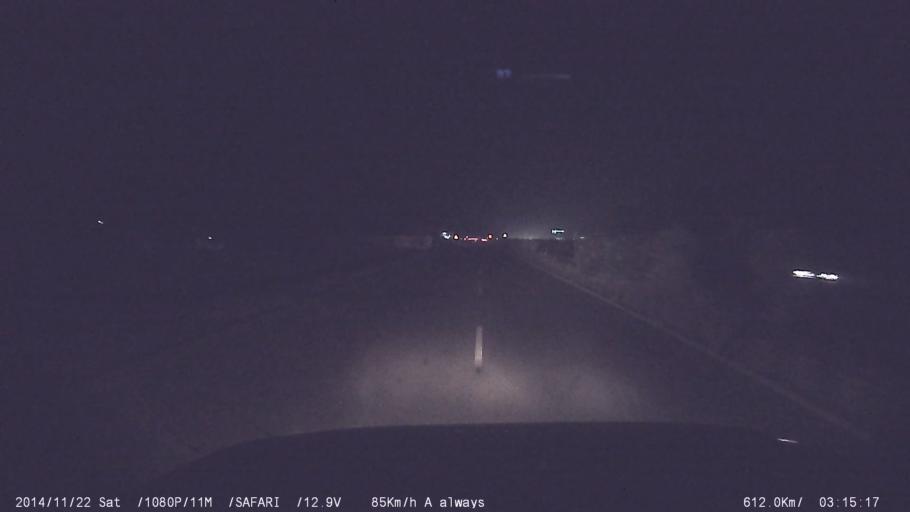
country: IN
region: Tamil Nadu
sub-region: Salem
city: Mallur
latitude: 11.6012
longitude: 78.0908
